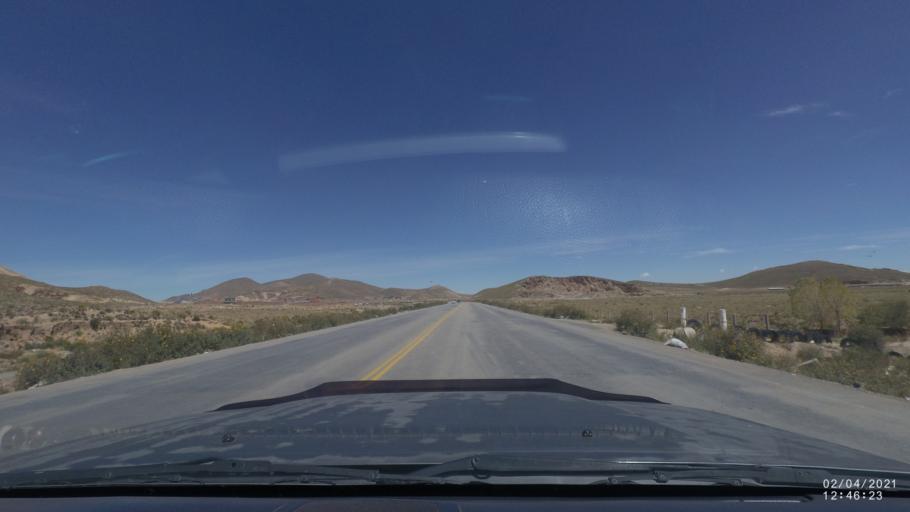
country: BO
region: Oruro
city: Oruro
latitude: -17.9445
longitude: -67.1414
